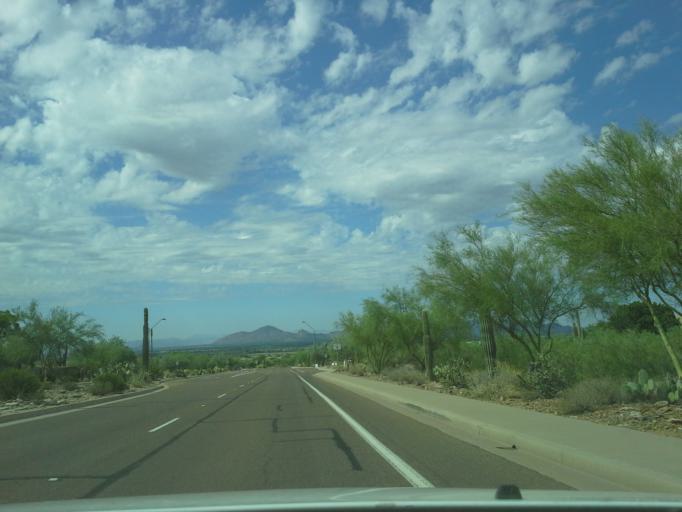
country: US
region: Arizona
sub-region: Maricopa County
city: Fountain Hills
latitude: 33.6341
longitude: -111.8463
